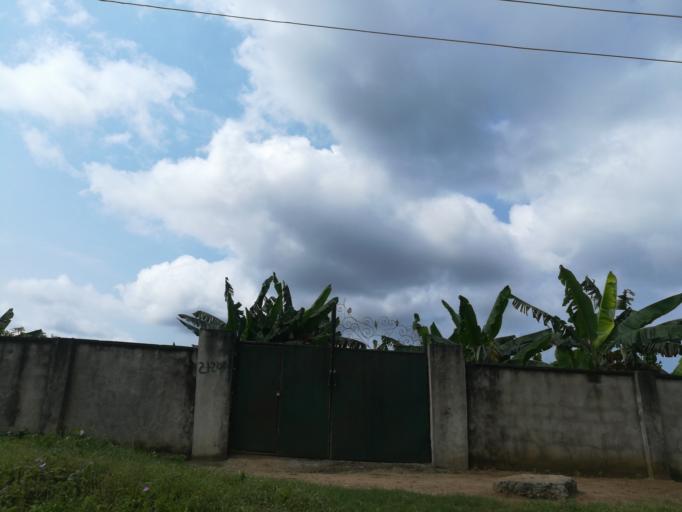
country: NG
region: Rivers
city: Okrika
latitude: 4.7419
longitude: 7.1163
